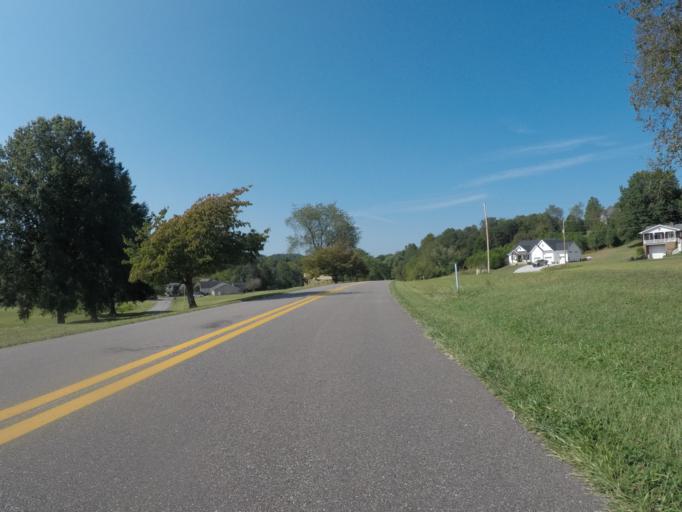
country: US
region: West Virginia
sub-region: Cabell County
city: Barboursville
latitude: 38.3657
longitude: -82.2677
